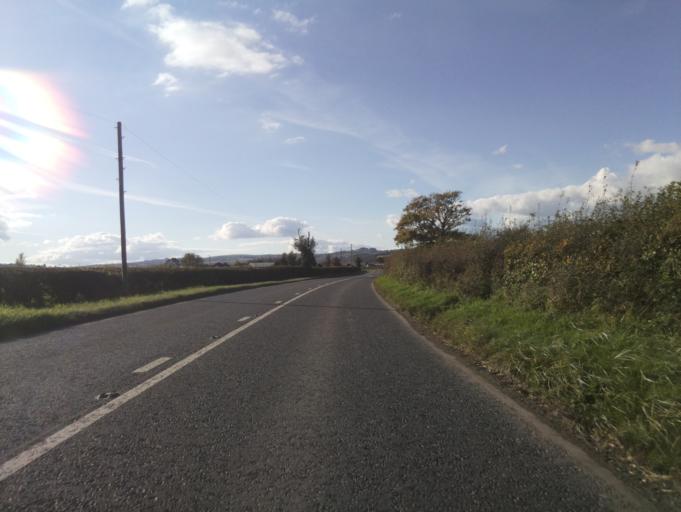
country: GB
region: England
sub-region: Herefordshire
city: Dorstone
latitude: 52.1171
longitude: -3.0341
